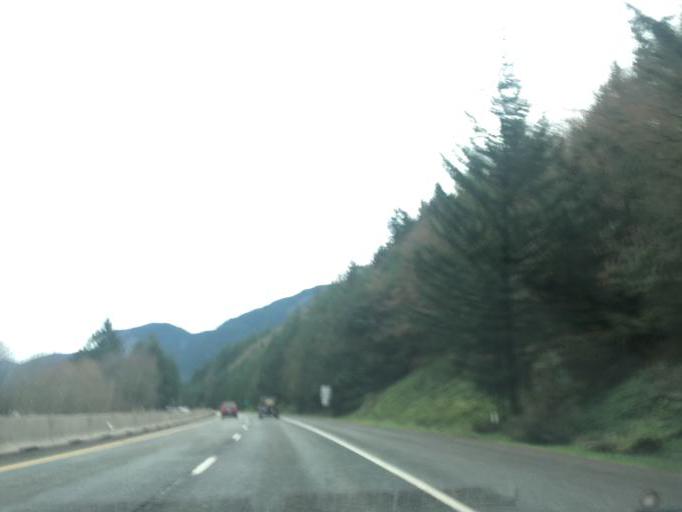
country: US
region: Washington
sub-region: Skamania County
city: Carson
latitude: 45.6947
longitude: -121.7955
